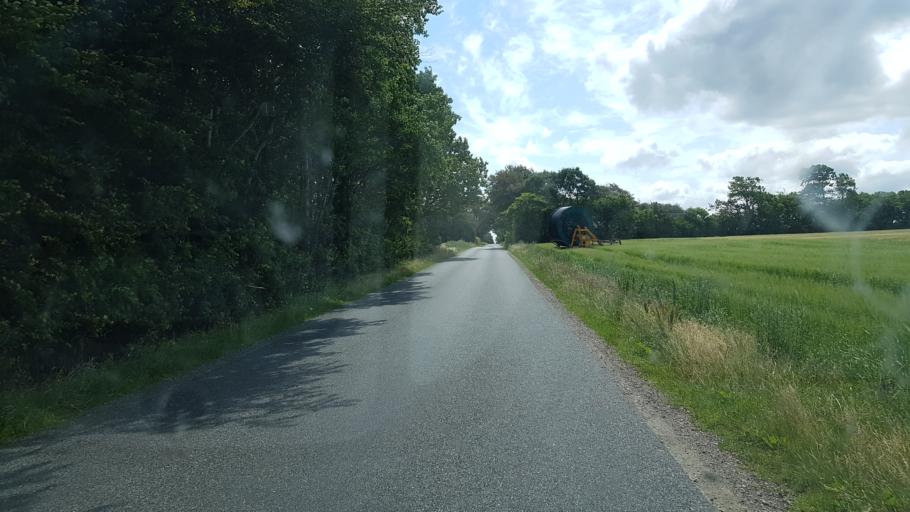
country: DK
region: South Denmark
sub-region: Vejen Kommune
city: Holsted
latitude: 55.4712
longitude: 8.9605
